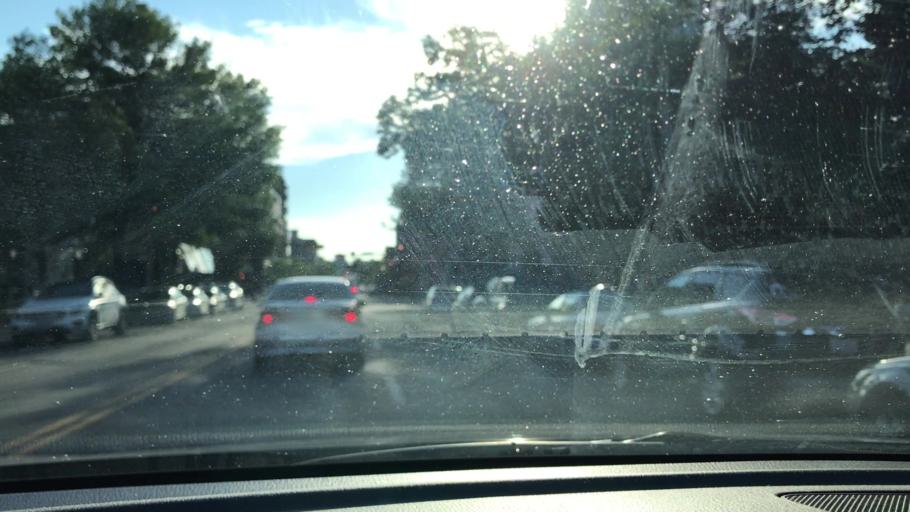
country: CA
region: Alberta
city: Calgary
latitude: 51.0379
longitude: -114.0804
